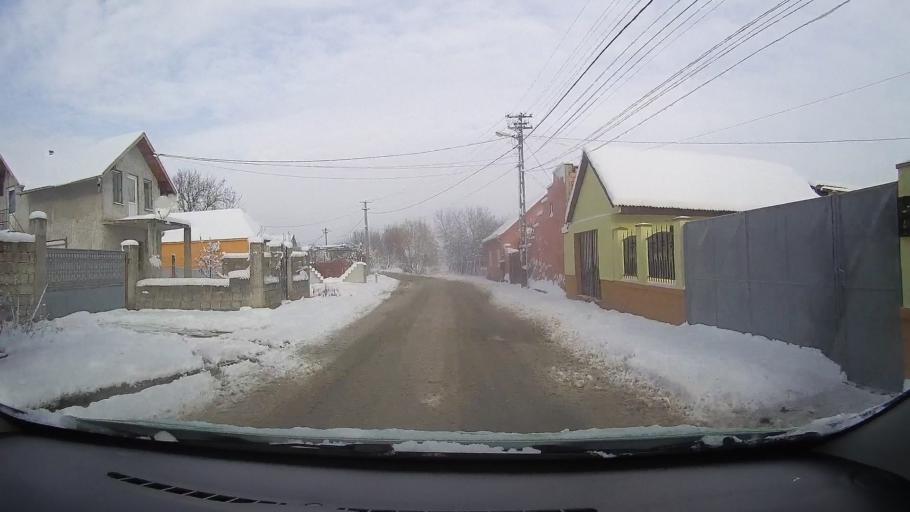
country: RO
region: Alba
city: Vurpar
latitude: 45.9794
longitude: 23.4821
